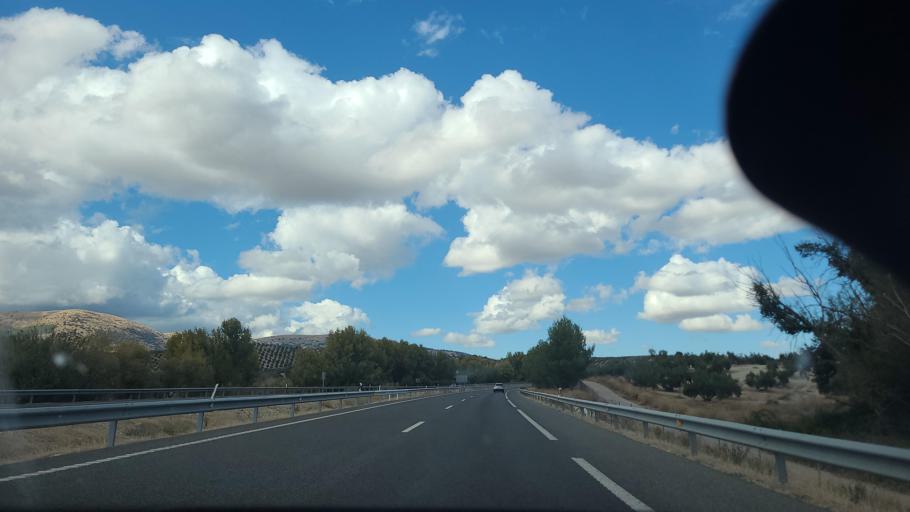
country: ES
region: Andalusia
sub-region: Provincia de Jaen
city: Noalejo
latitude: 37.5125
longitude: -3.6359
